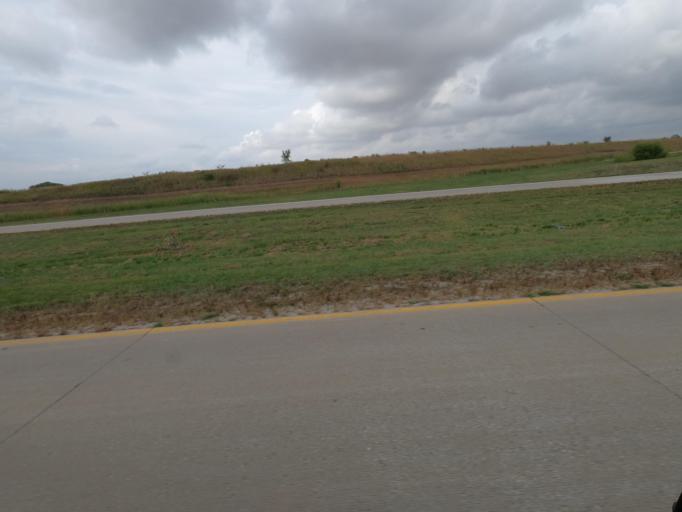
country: US
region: Iowa
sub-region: Wapello County
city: Ottumwa
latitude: 41.0033
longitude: -92.3080
